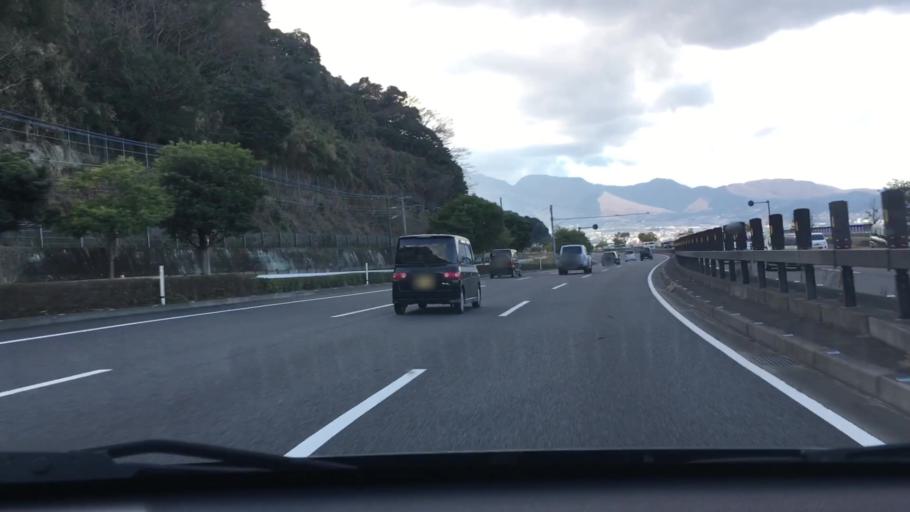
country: JP
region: Oita
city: Oita
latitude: 33.2511
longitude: 131.5704
